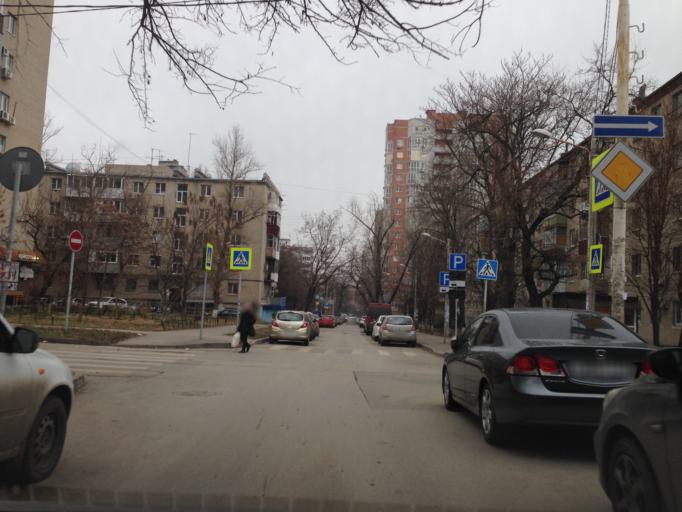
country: RU
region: Rostov
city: Rostov-na-Donu
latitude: 47.2306
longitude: 39.7120
